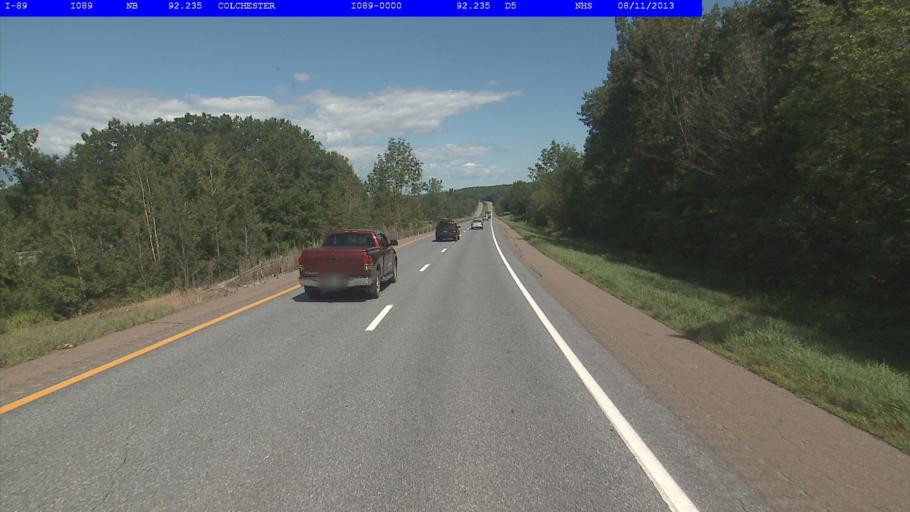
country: US
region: Vermont
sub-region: Chittenden County
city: Winooski
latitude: 44.5130
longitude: -73.1912
